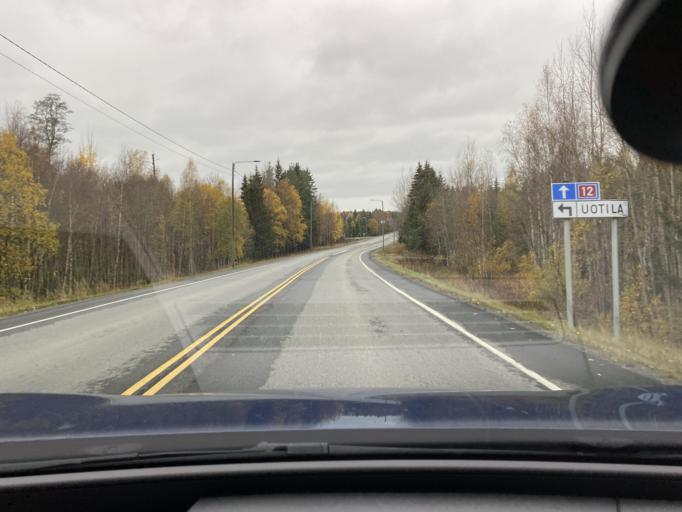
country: FI
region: Satakunta
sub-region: Rauma
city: Rauma
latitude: 61.1276
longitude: 21.6072
